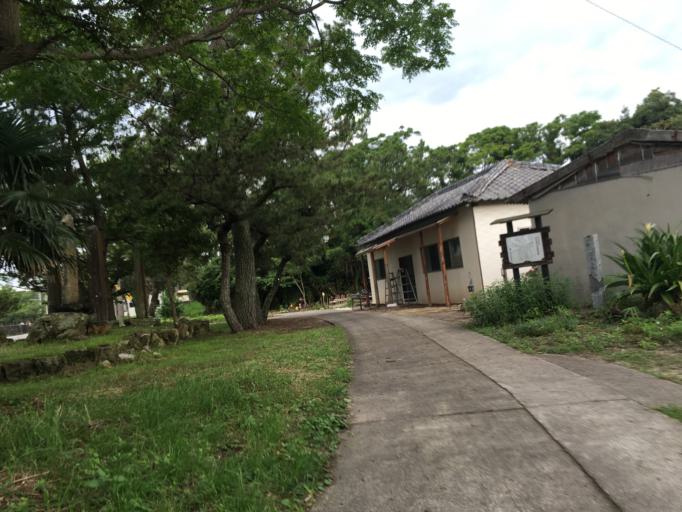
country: JP
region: Aichi
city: Ishiki
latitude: 34.7264
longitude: 137.0447
